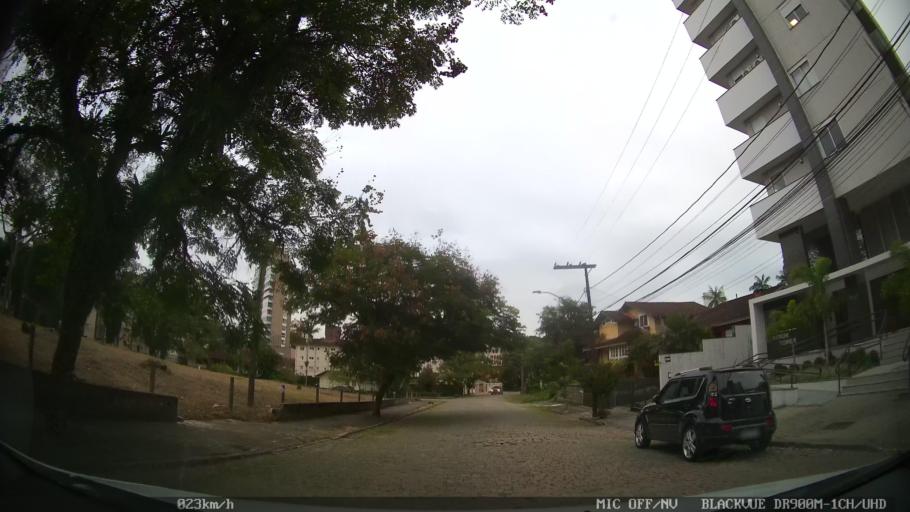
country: BR
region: Santa Catarina
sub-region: Joinville
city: Joinville
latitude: -26.3092
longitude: -48.8591
